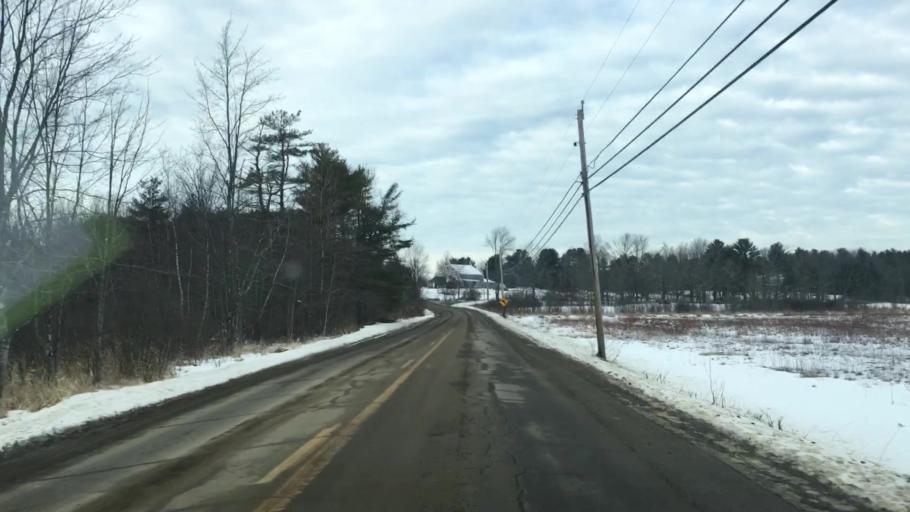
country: US
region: Maine
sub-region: Lincoln County
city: Whitefield
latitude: 44.2339
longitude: -69.6167
